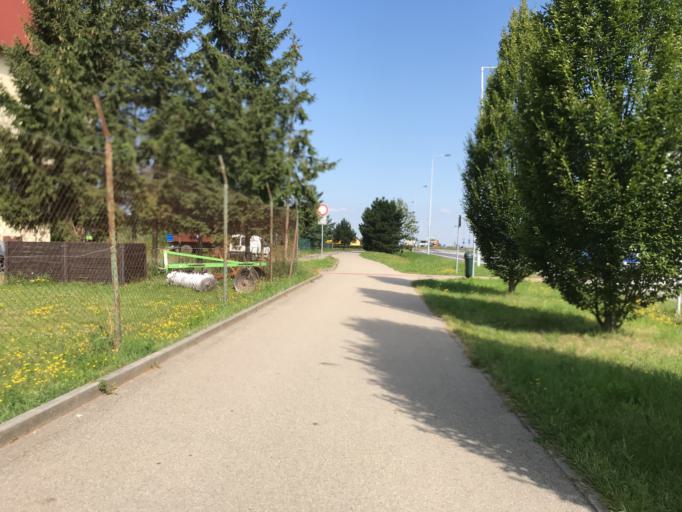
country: CZ
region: Jihocesky
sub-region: Okres Jindrichuv Hradec
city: Trebon
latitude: 49.0119
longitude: 14.7582
